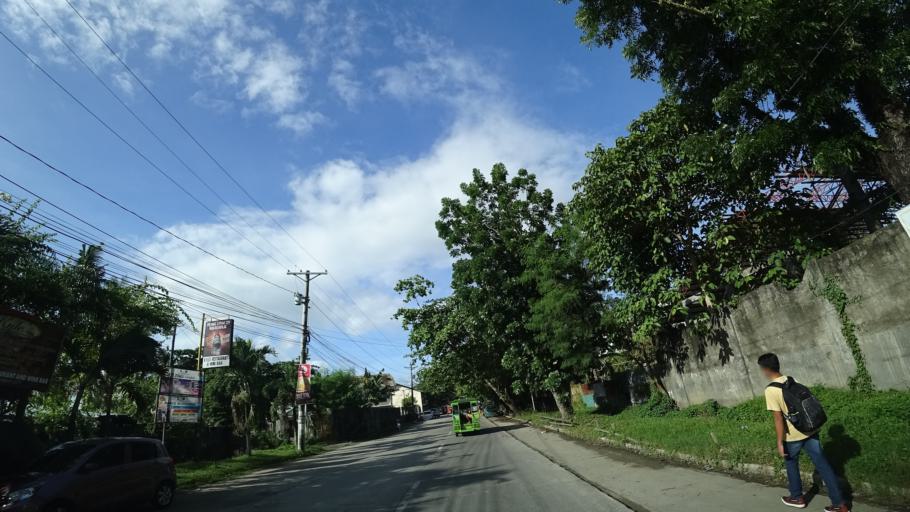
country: PH
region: Eastern Visayas
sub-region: Province of Leyte
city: Panalanoy
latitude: 11.2364
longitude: 125.0009
